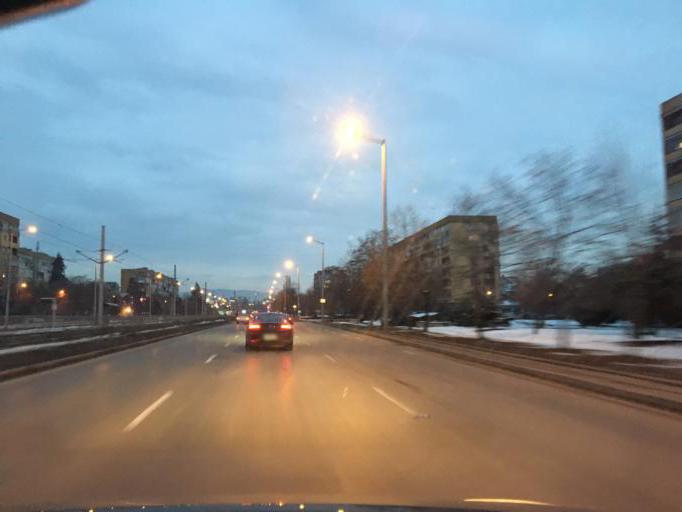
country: BG
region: Sofia-Capital
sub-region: Stolichna Obshtina
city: Sofia
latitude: 42.6998
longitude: 23.3678
